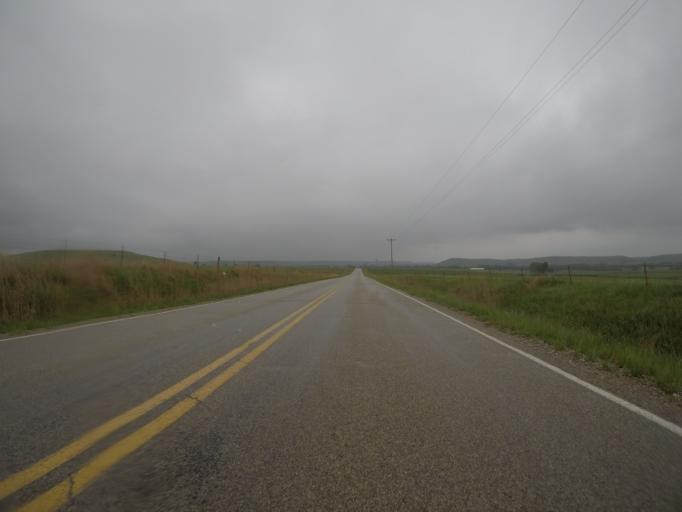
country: US
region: Kansas
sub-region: Pottawatomie County
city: Westmoreland
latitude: 39.4124
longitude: -96.1839
